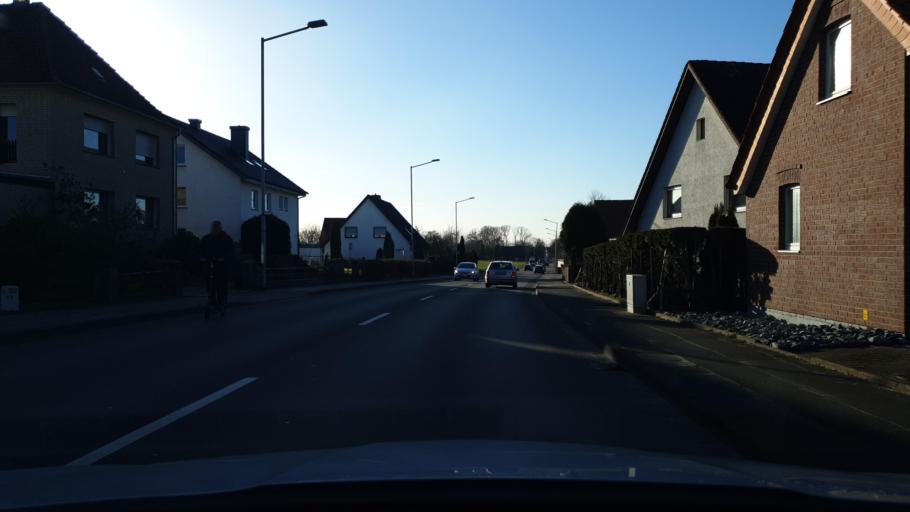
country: DE
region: North Rhine-Westphalia
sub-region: Regierungsbezirk Detmold
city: Kirchlengern
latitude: 52.2049
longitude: 8.6645
